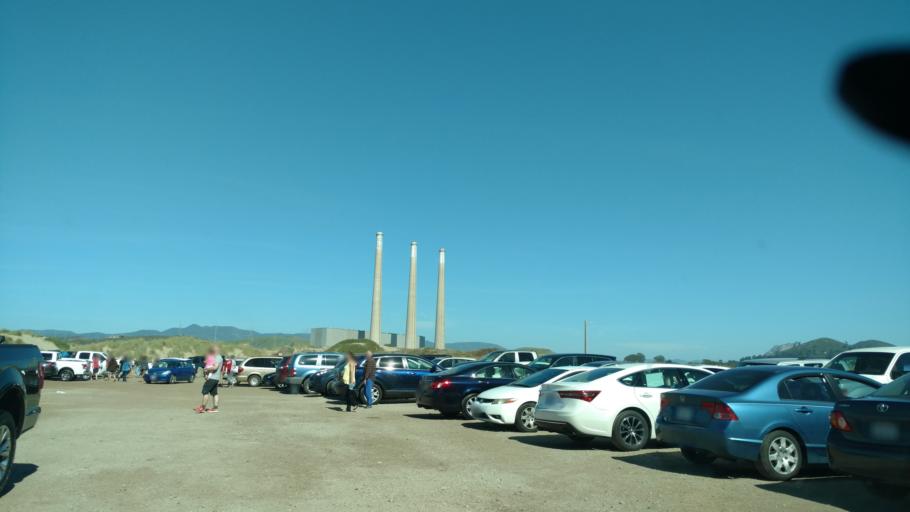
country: US
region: California
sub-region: San Luis Obispo County
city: Morro Bay
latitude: 35.3711
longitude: -120.8650
